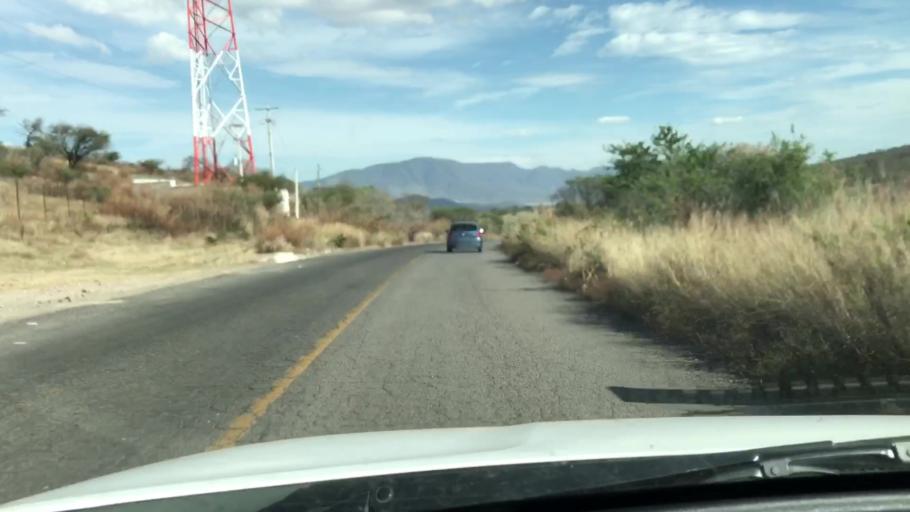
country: MX
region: Jalisco
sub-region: Zacoalco de Torres
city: Barranca de Otates (Barranca de Otatan)
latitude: 20.2589
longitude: -103.6582
